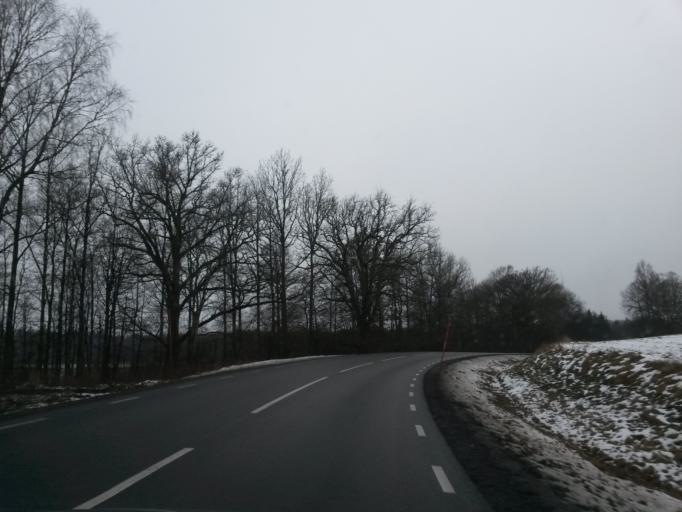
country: SE
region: Vaestra Goetaland
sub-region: Tranemo Kommun
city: Langhem
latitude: 57.6866
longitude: 13.3088
